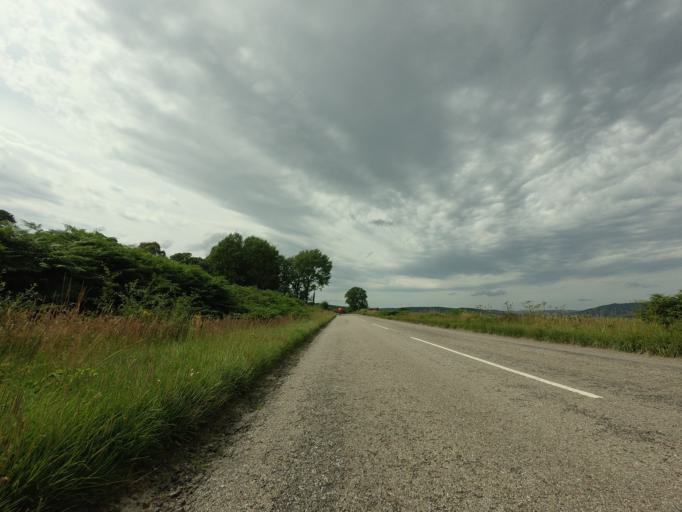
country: GB
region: Scotland
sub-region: Highland
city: Alness
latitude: 57.8701
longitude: -4.3438
